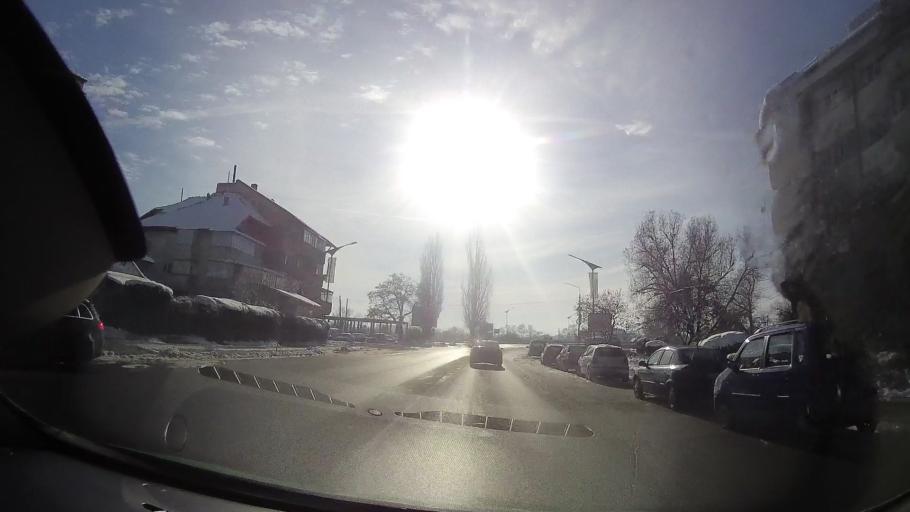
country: RO
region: Neamt
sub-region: Oras Targu Neamt
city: Humulesti
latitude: 47.2023
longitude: 26.3580
